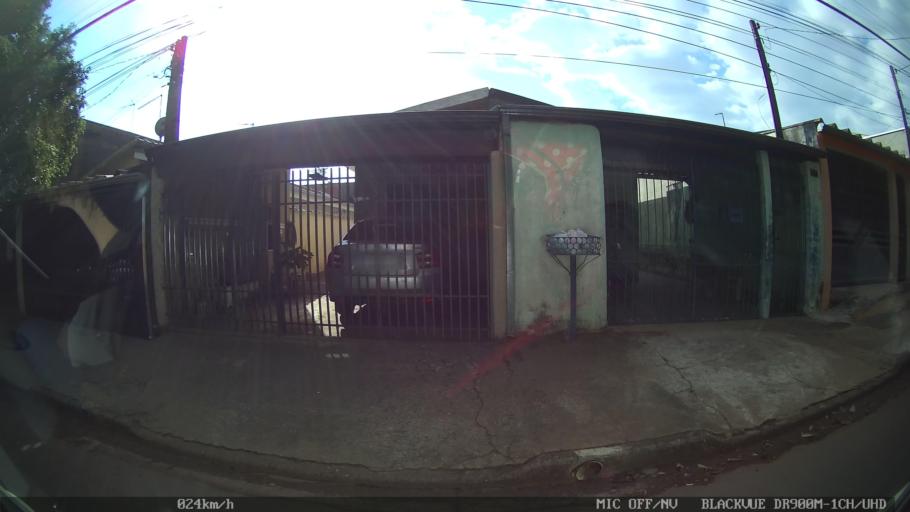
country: BR
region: Sao Paulo
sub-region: Americana
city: Americana
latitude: -22.7156
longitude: -47.3686
